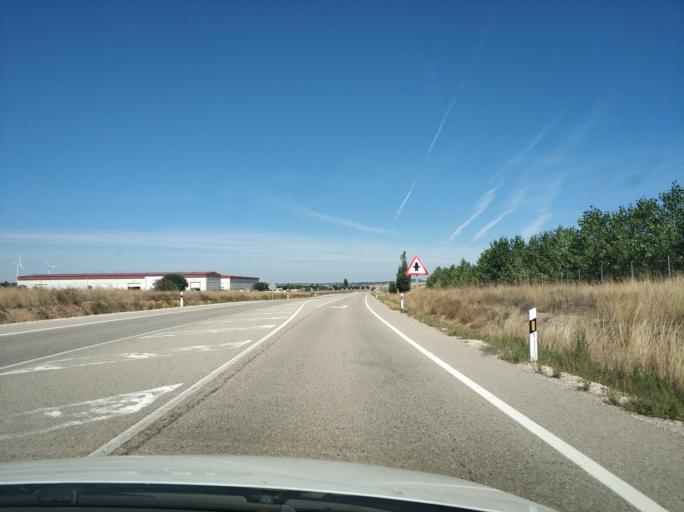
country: ES
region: Castille and Leon
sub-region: Provincia de Burgos
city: Hontoria de la Cantera
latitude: 42.2019
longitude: -3.6483
